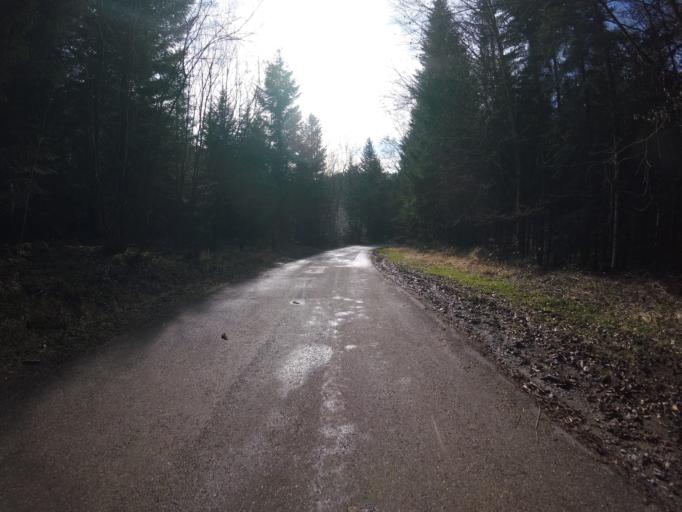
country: DE
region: Baden-Wuerttemberg
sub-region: Regierungsbezirk Stuttgart
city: Murrhardt
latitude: 48.9867
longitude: 9.6075
